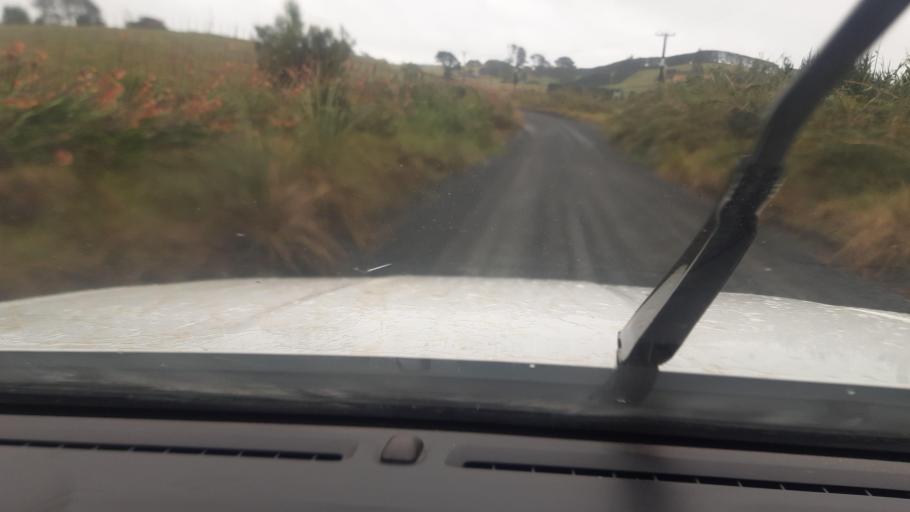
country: NZ
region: Northland
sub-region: Far North District
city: Kaitaia
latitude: -34.9790
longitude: 173.1980
